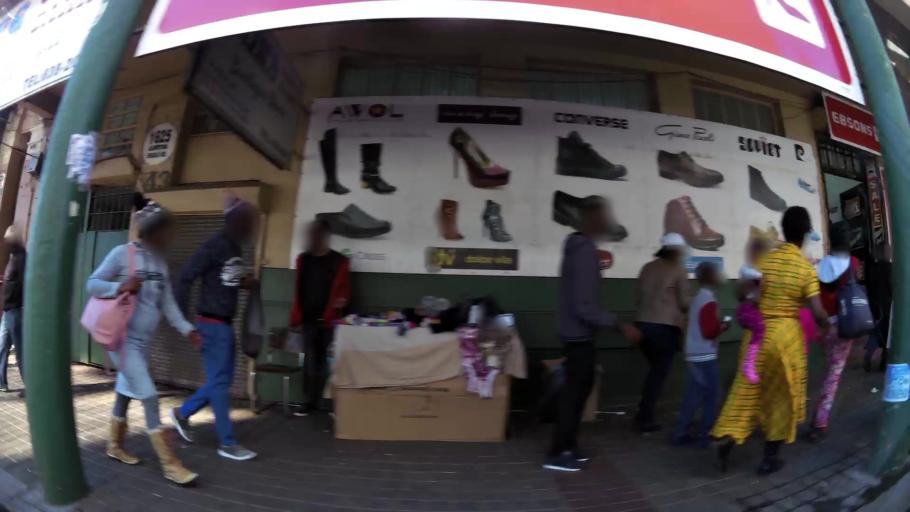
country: ZA
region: Gauteng
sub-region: City of Johannesburg Metropolitan Municipality
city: Johannesburg
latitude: -26.2053
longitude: 28.0365
